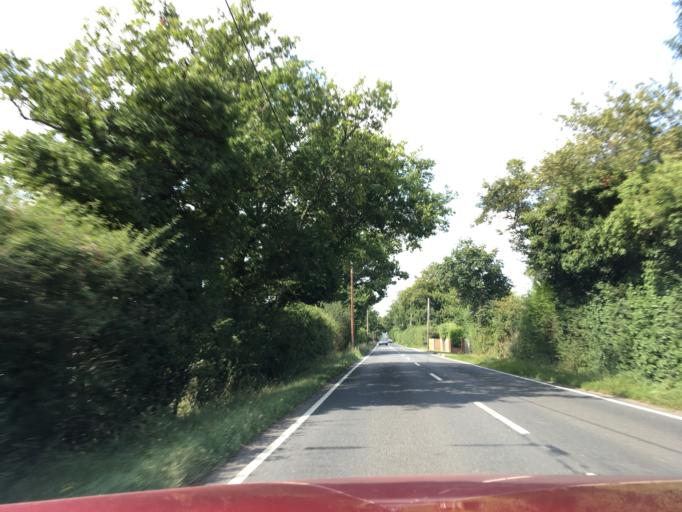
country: GB
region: England
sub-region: Kent
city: Headcorn
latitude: 51.1522
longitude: 0.6368
